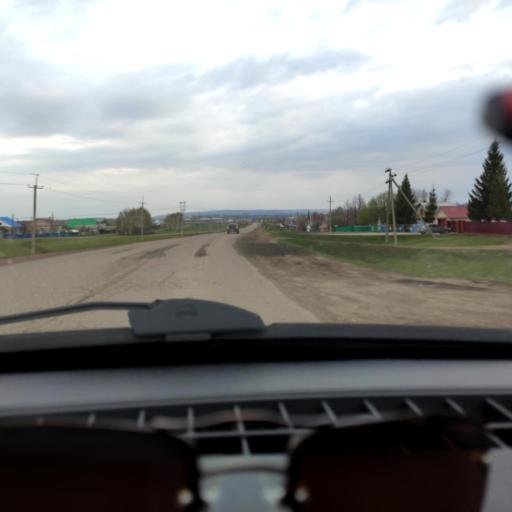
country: RU
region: Bashkortostan
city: Kabakovo
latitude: 54.5346
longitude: 56.1447
